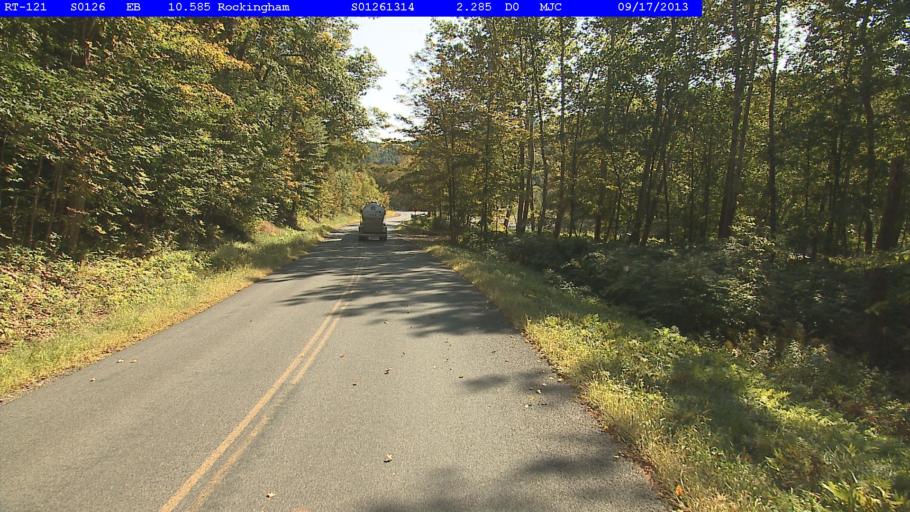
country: US
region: Vermont
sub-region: Windham County
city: Rockingham
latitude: 43.1352
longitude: -72.5200
